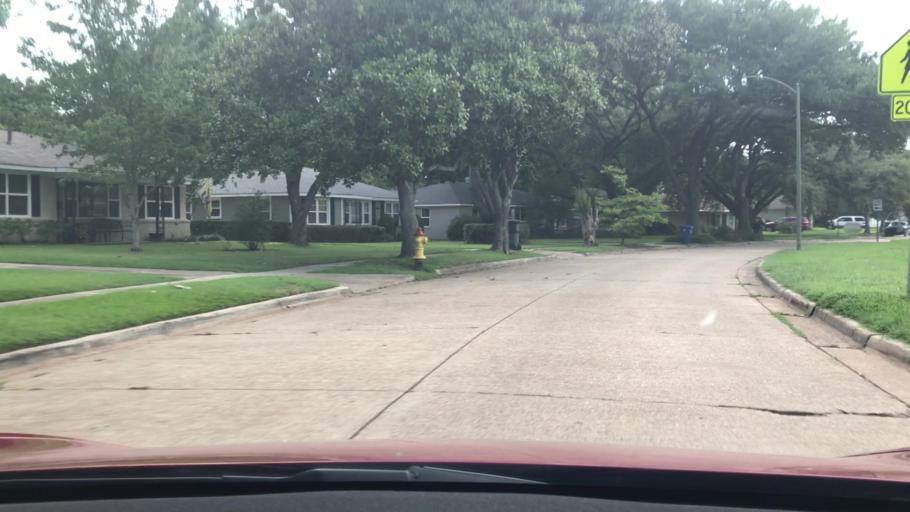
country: US
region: Louisiana
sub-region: Bossier Parish
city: Bossier City
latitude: 32.4585
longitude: -93.7177
